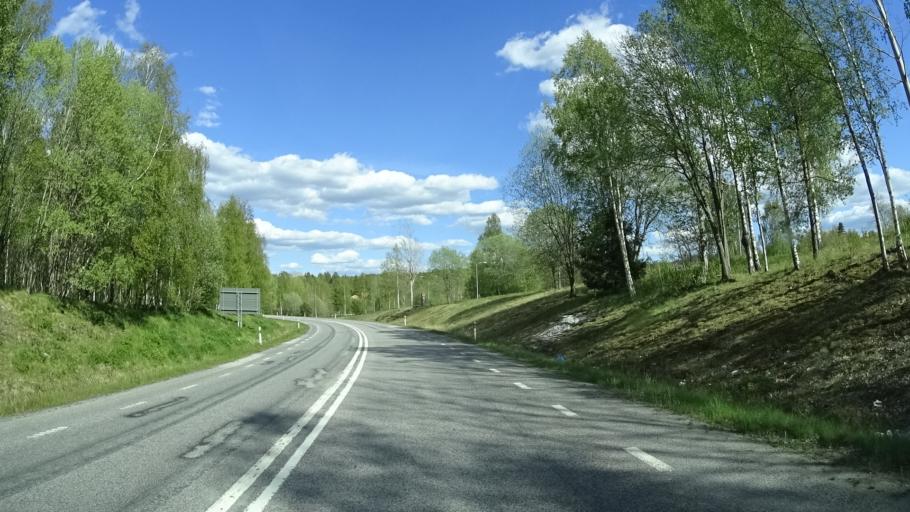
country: SE
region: OErebro
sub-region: Nora Kommun
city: As
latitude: 59.5071
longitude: 14.9694
